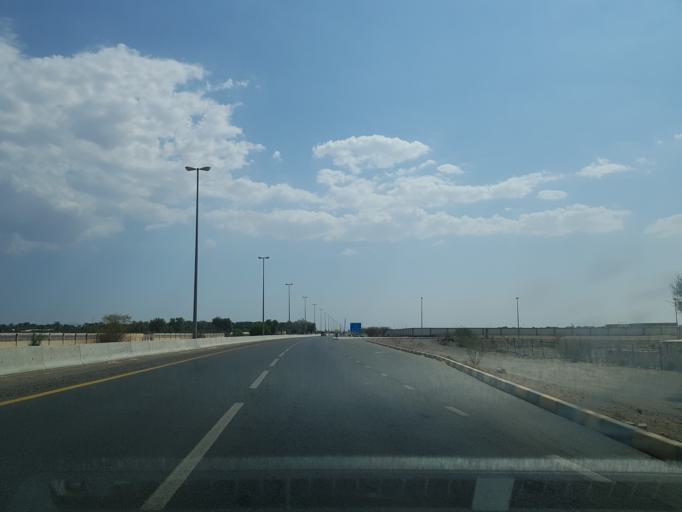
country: AE
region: Ash Shariqah
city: Adh Dhayd
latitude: 25.2384
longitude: 55.9161
